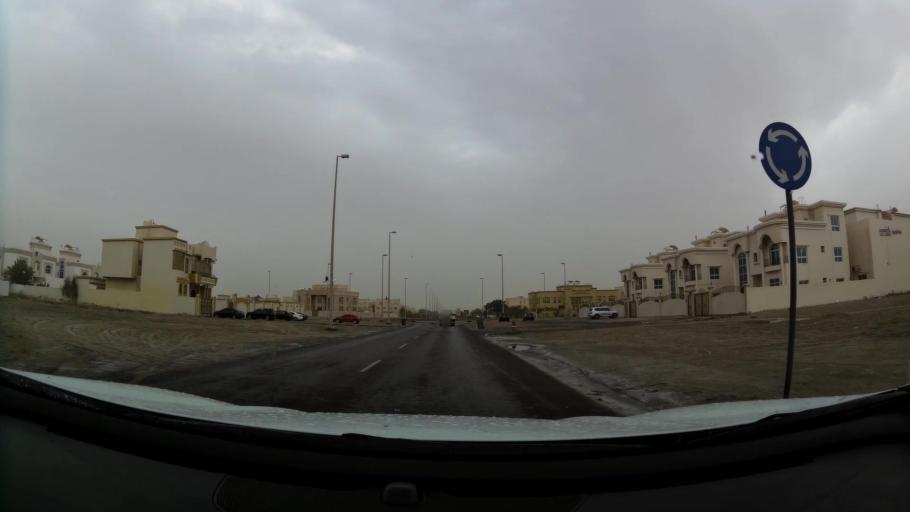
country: AE
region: Abu Dhabi
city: Abu Dhabi
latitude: 24.4122
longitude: 54.5864
